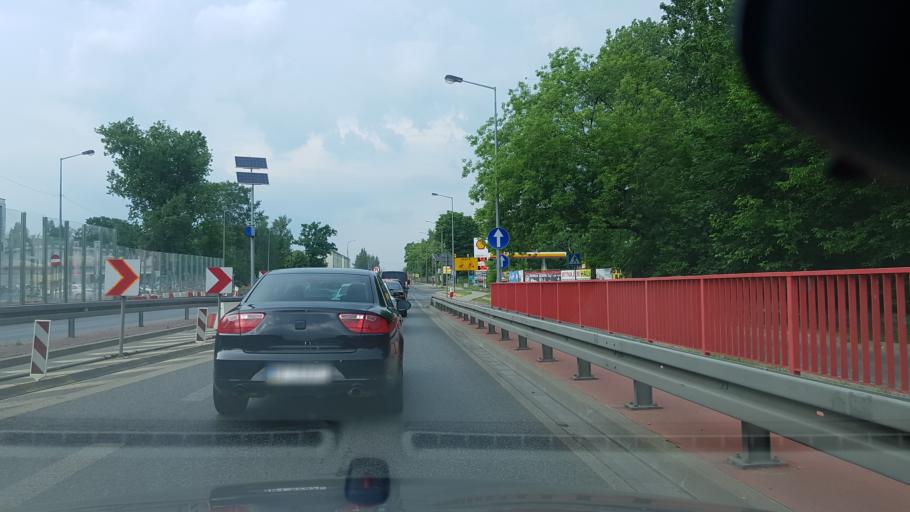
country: PL
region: Masovian Voivodeship
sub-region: Powiat legionowski
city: Legionowo
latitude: 52.4017
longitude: 20.9465
